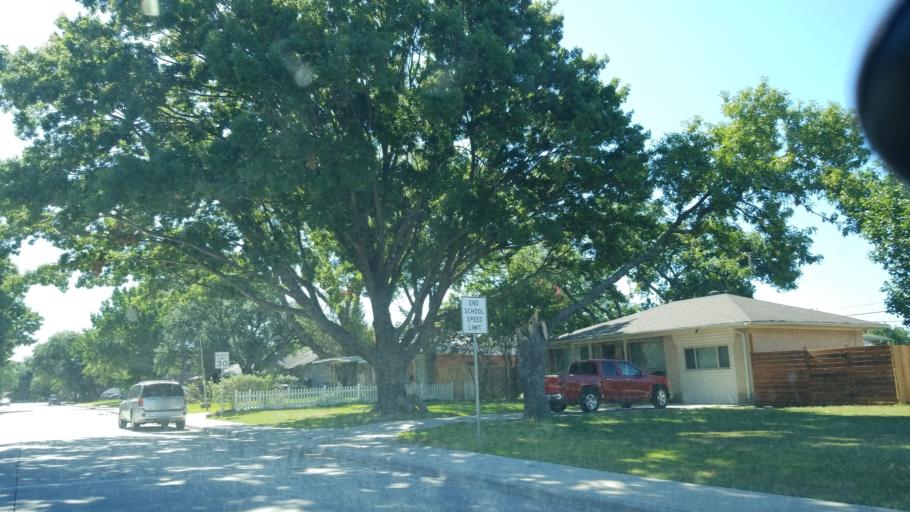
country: US
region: Texas
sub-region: Dallas County
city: Carrollton
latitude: 32.9580
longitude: -96.8926
